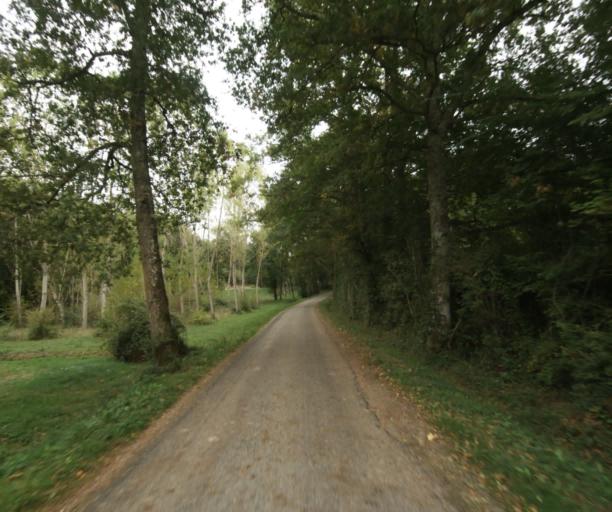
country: FR
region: Midi-Pyrenees
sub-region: Departement du Gers
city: Eauze
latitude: 43.8930
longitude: 0.1266
